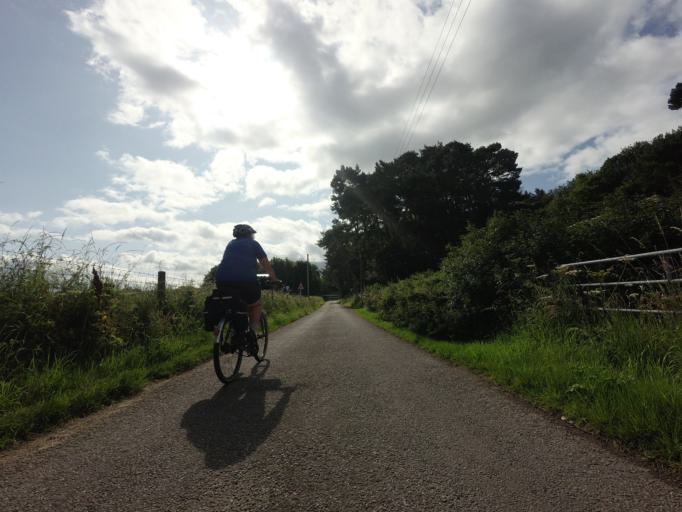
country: GB
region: Scotland
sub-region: Highland
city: Nairn
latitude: 57.5689
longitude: -3.8672
